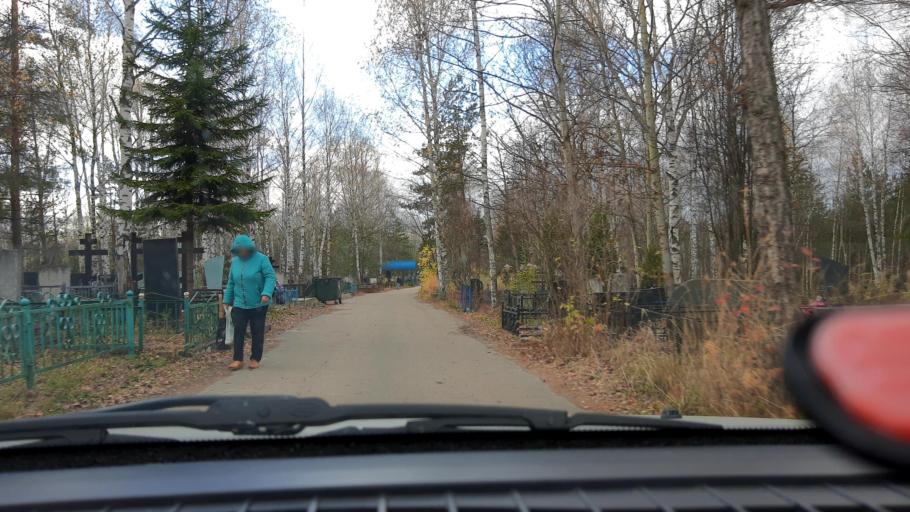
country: RU
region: Nizjnij Novgorod
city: Gorbatovka
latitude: 56.3606
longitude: 43.7850
